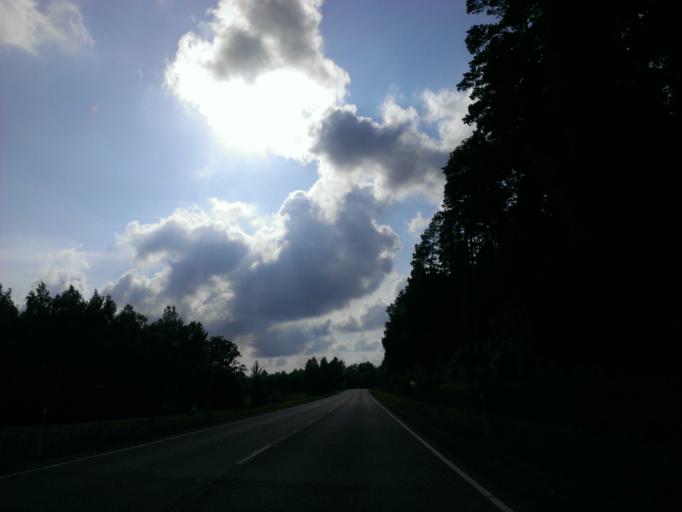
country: LV
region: Priekuli
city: Priekuli
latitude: 57.2935
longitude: 25.4722
